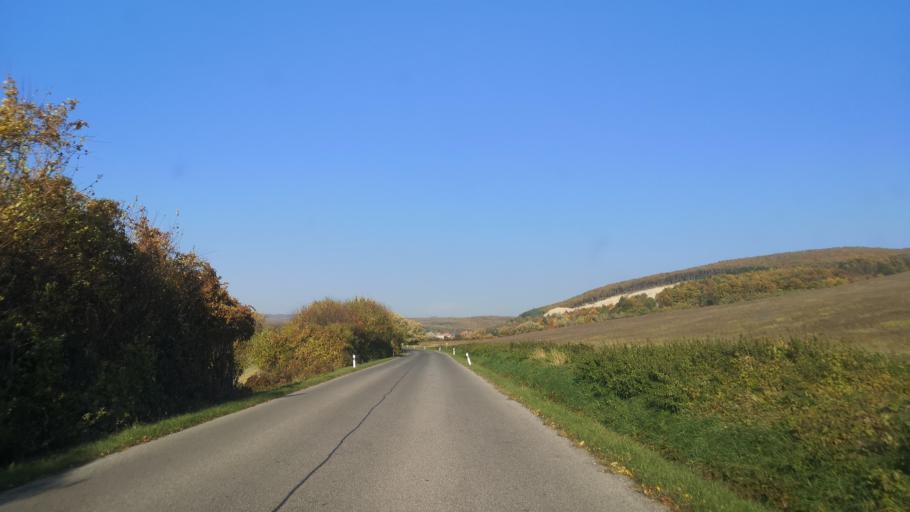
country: SK
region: Nitriansky
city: Zlate Moravce
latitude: 48.4395
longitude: 18.4310
